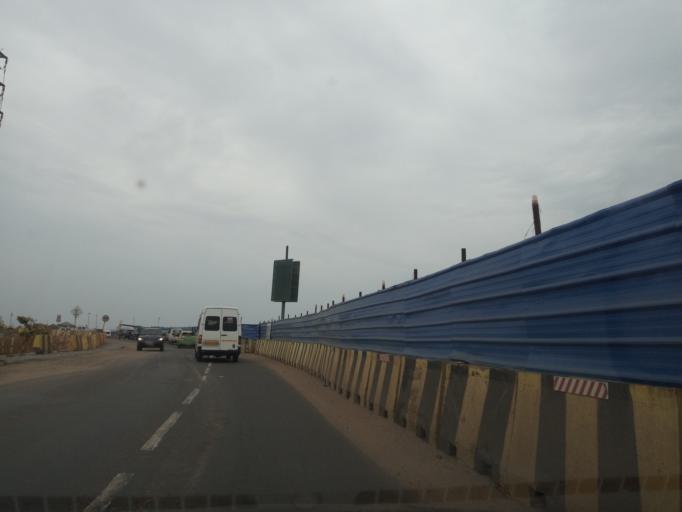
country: GH
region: Greater Accra
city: Tema
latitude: 5.6183
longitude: -0.0228
